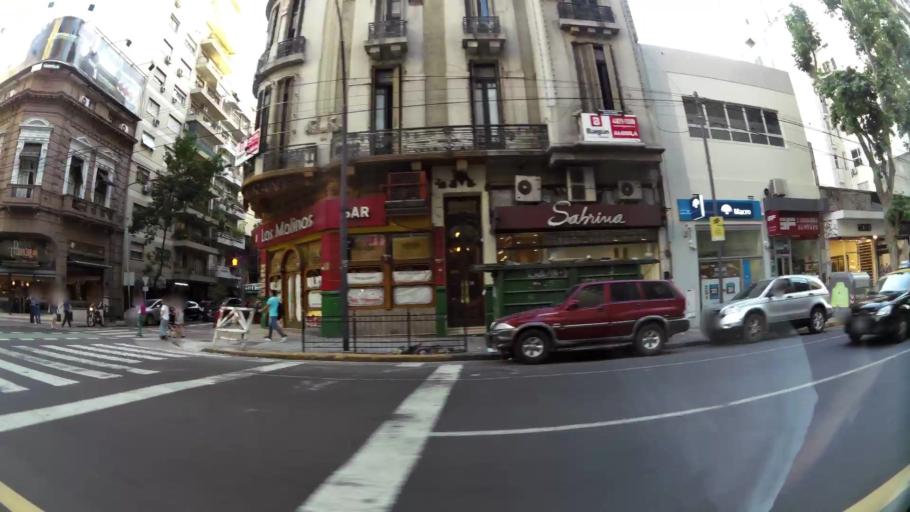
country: AR
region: Buenos Aires F.D.
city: Retiro
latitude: -34.5953
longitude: -58.3988
